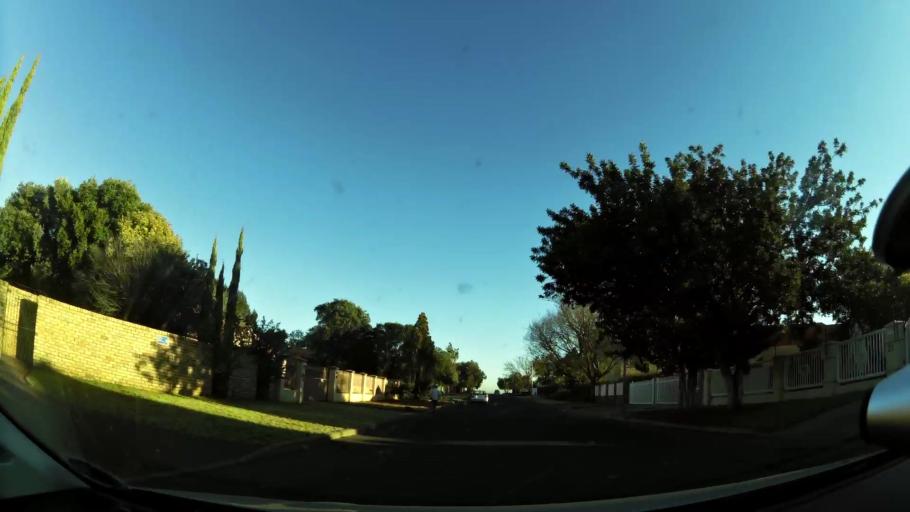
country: ZA
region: Northern Cape
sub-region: Frances Baard District Municipality
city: Kimberley
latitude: -28.7579
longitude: 24.7338
